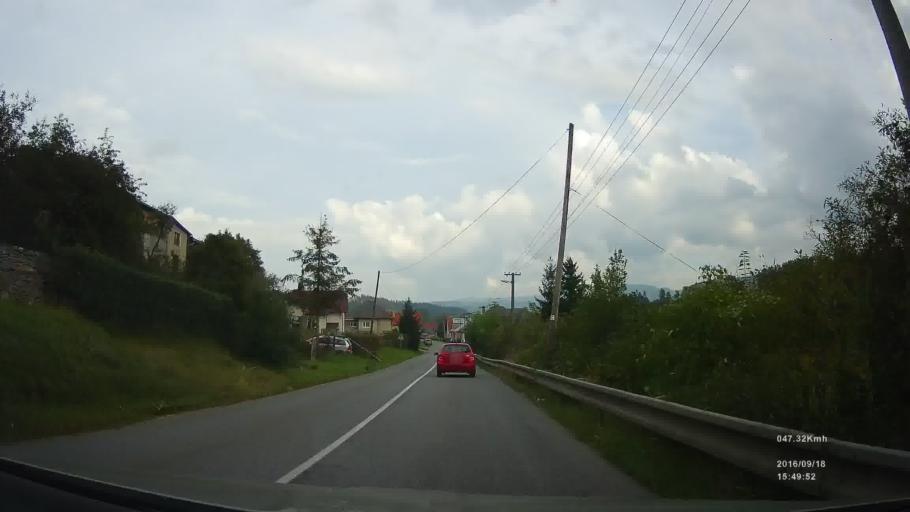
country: SK
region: Kosicky
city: Spisska Nova Ves
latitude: 48.9150
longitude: 20.6129
